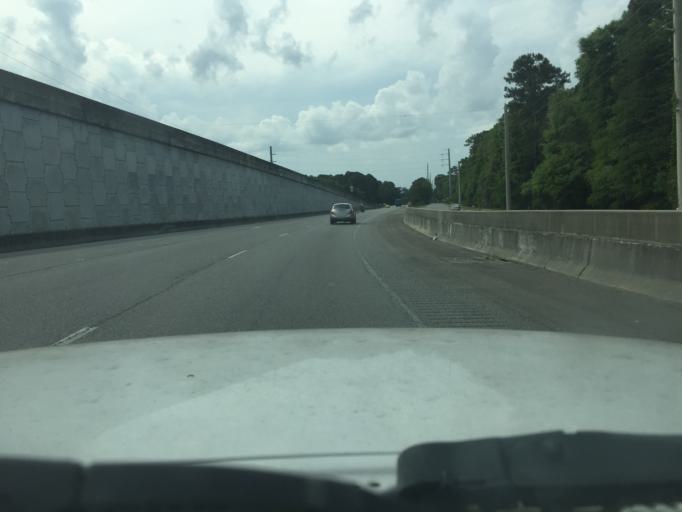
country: US
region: Georgia
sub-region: Chatham County
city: Whitemarsh Island
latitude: 32.0448
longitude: -81.0047
